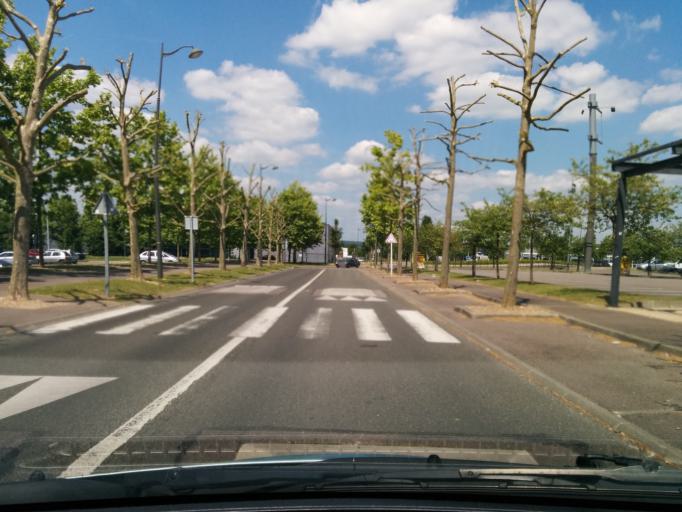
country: FR
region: Ile-de-France
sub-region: Departement des Yvelines
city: Buchelay
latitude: 48.9904
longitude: 1.6736
